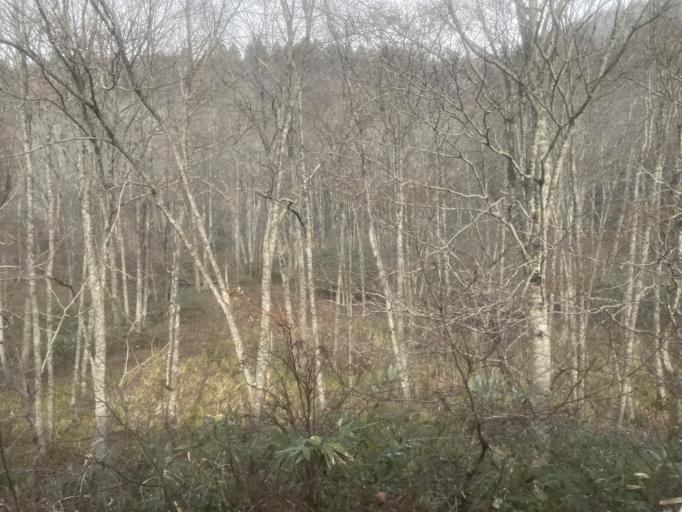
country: JP
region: Aomori
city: Goshogawara
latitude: 41.0812
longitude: 140.5241
